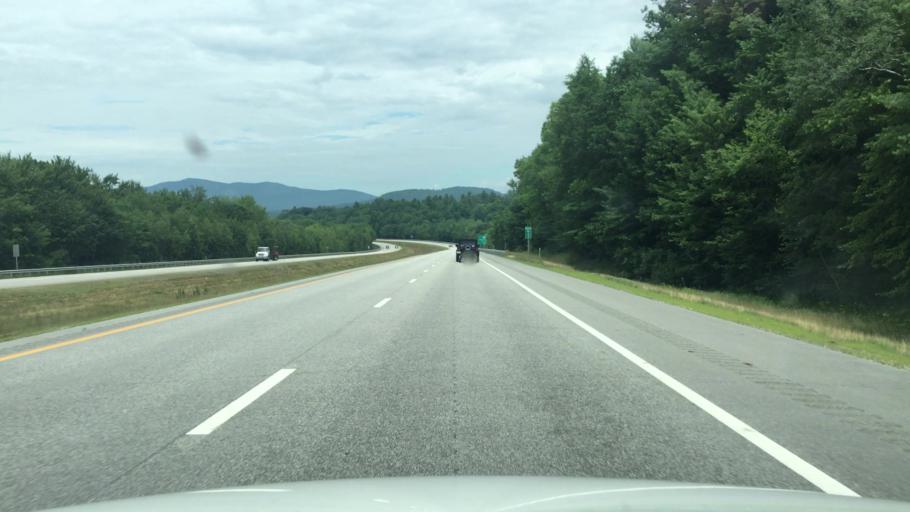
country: US
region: New Hampshire
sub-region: Grafton County
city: Plymouth
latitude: 43.7457
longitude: -71.6634
